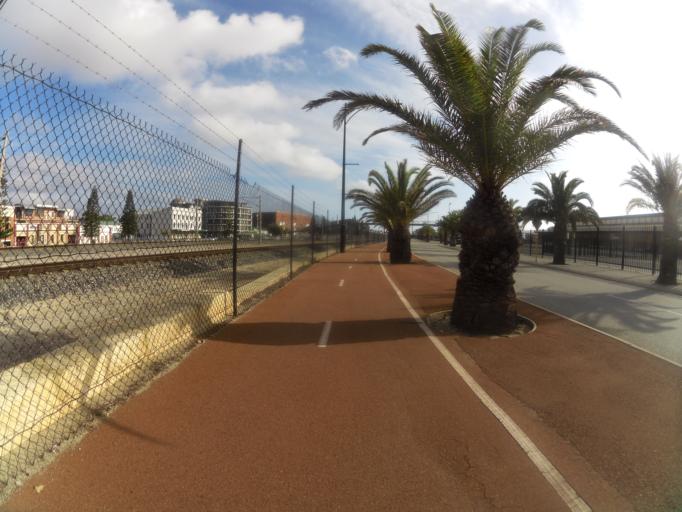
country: AU
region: Western Australia
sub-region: Fremantle
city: North Fremantle
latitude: -32.0476
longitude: 115.7491
